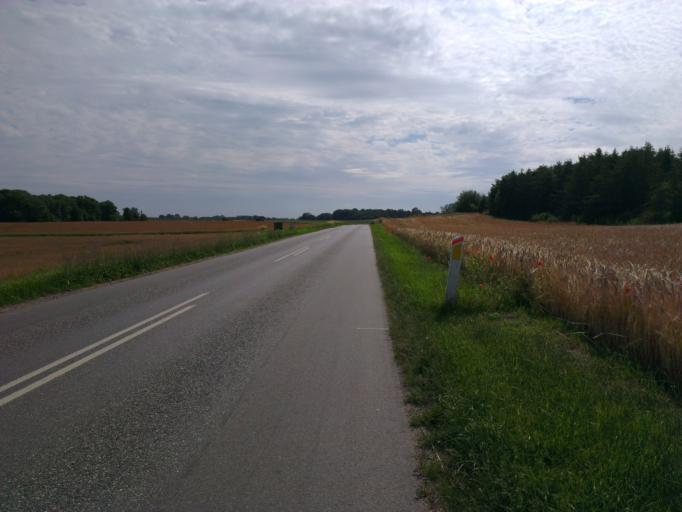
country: DK
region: Capital Region
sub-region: Frederikssund Kommune
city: Skibby
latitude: 55.7937
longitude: 12.0133
